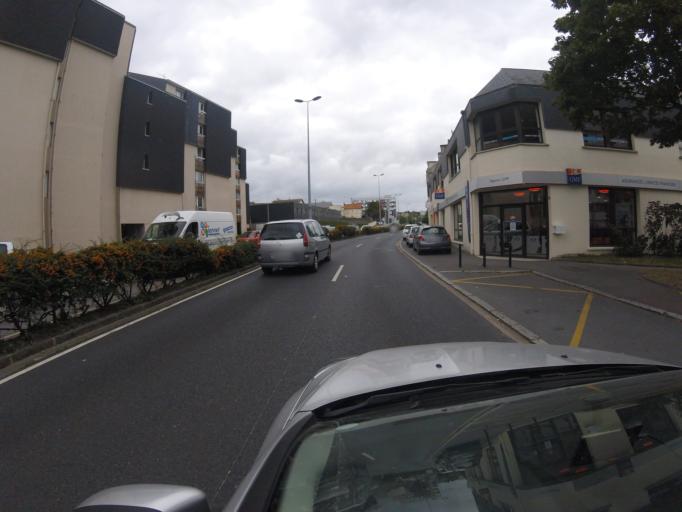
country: FR
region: Lower Normandy
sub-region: Departement de la Manche
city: Cherbourg-Octeville
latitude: 49.6340
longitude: -1.6233
